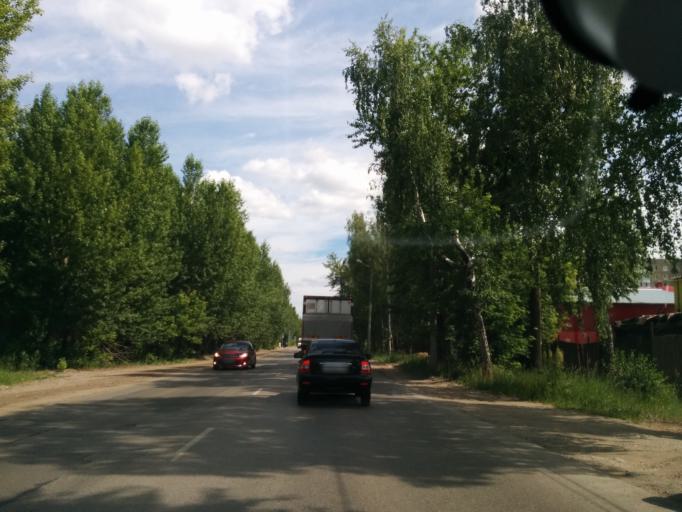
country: RU
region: Perm
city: Overyata
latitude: 58.0129
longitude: 55.9547
